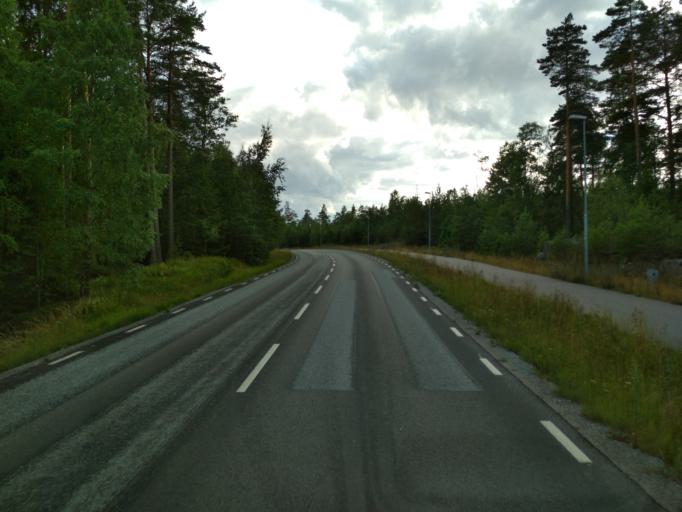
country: SE
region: Stockholm
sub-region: Sigtuna Kommun
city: Sigtuna
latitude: 59.6847
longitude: 17.6026
